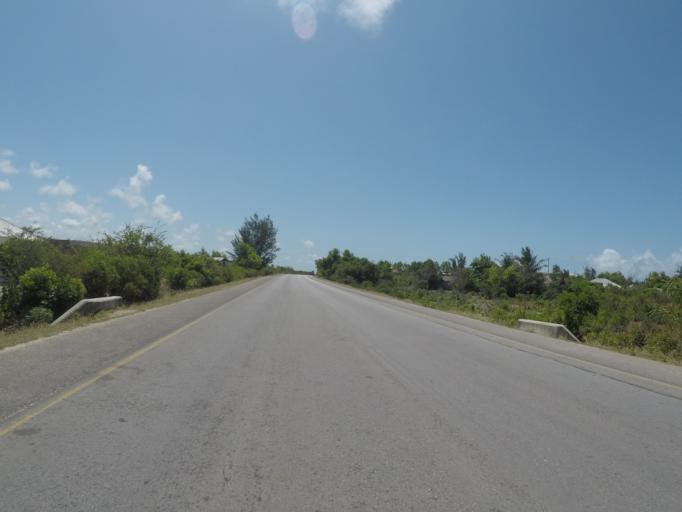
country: TZ
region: Zanzibar Central/South
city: Nganane
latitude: -6.3065
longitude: 39.5398
